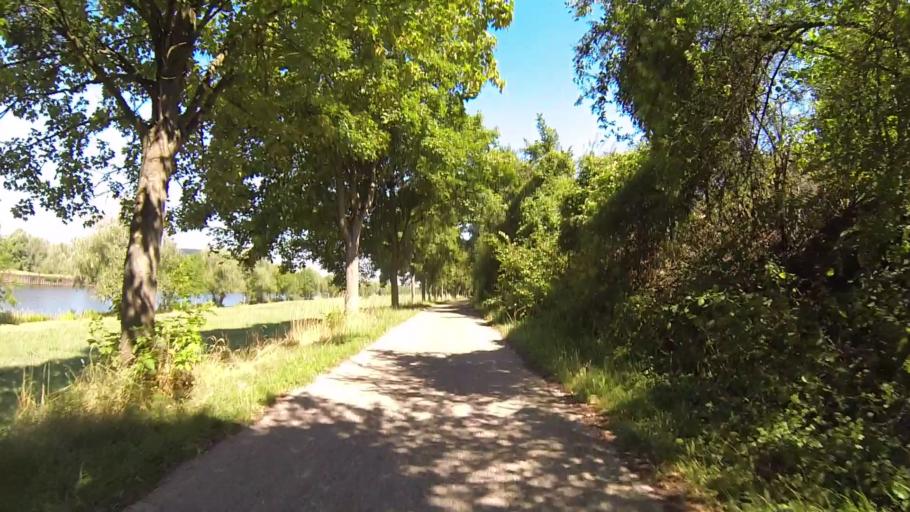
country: LU
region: Grevenmacher
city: Schengen
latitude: 49.4920
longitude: 6.3692
